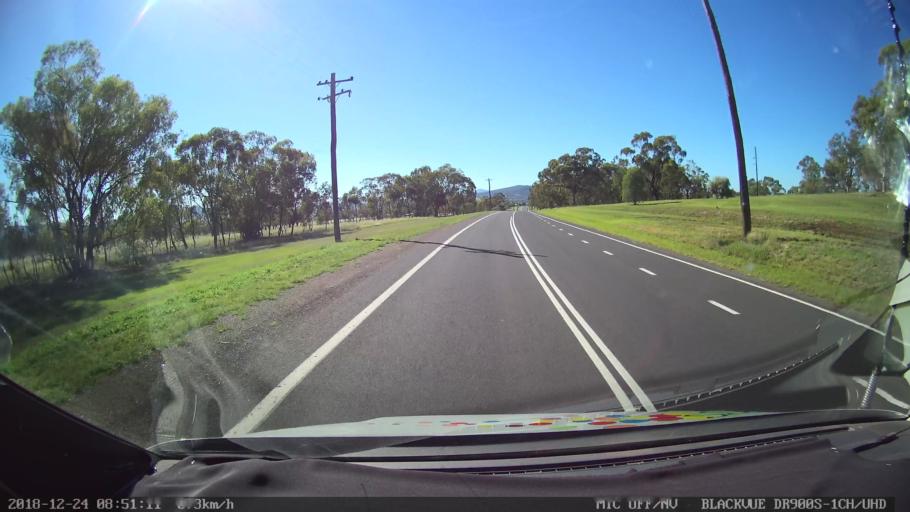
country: AU
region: New South Wales
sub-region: Liverpool Plains
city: Quirindi
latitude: -31.4822
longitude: 150.6721
